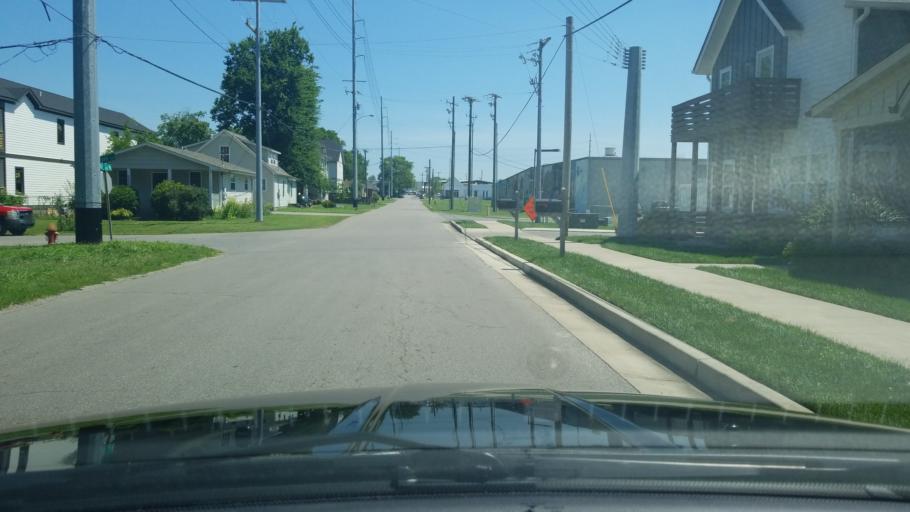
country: US
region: Tennessee
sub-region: Davidson County
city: Belle Meade
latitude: 36.1630
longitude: -86.8607
